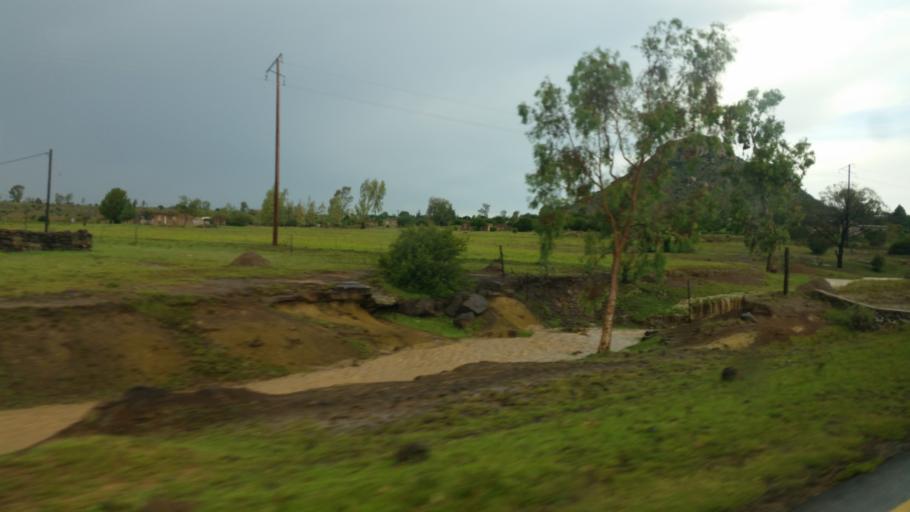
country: LS
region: Mafeteng
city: Mafeteng
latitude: -29.7591
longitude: 27.1728
